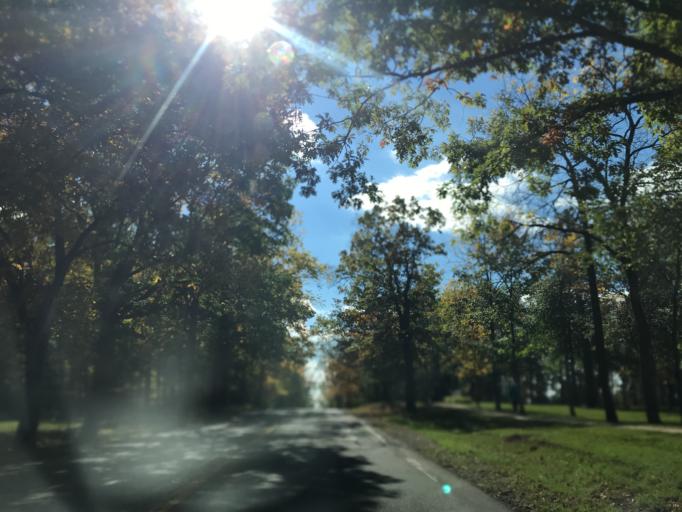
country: US
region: Michigan
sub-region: Washtenaw County
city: Ann Arbor
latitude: 42.2804
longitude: -83.6823
